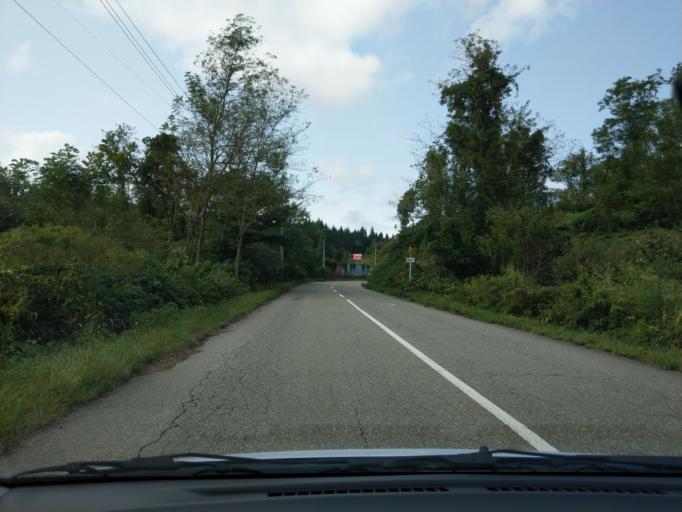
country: JP
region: Akita
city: Omagari
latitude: 39.5199
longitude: 140.2989
